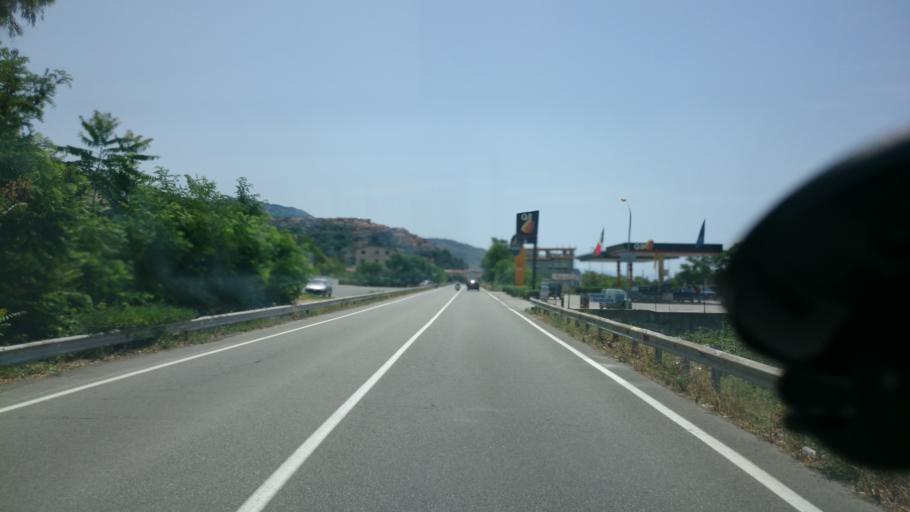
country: IT
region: Calabria
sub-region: Provincia di Cosenza
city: Cetraro Marina
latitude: 39.5264
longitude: 15.9282
